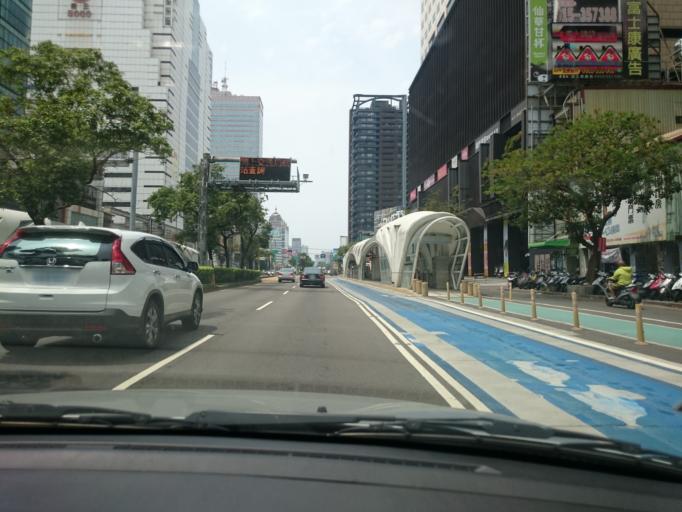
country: TW
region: Taiwan
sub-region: Taichung City
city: Taichung
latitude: 24.1551
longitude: 120.6635
